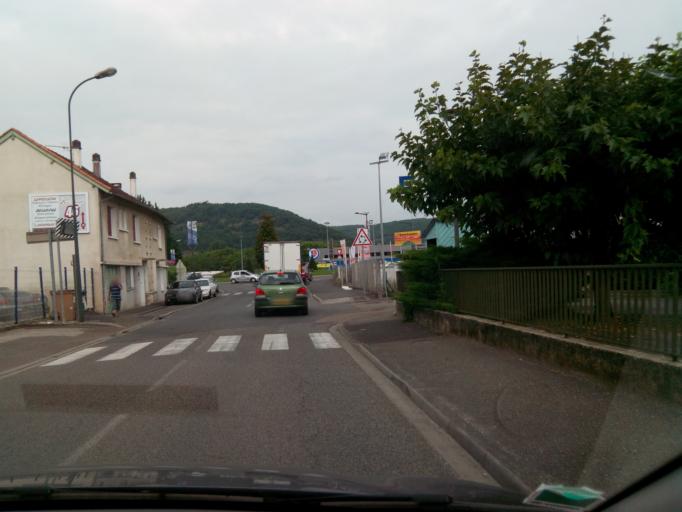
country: FR
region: Midi-Pyrenees
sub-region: Departement du Lot
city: Souillac
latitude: 44.8974
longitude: 1.4637
